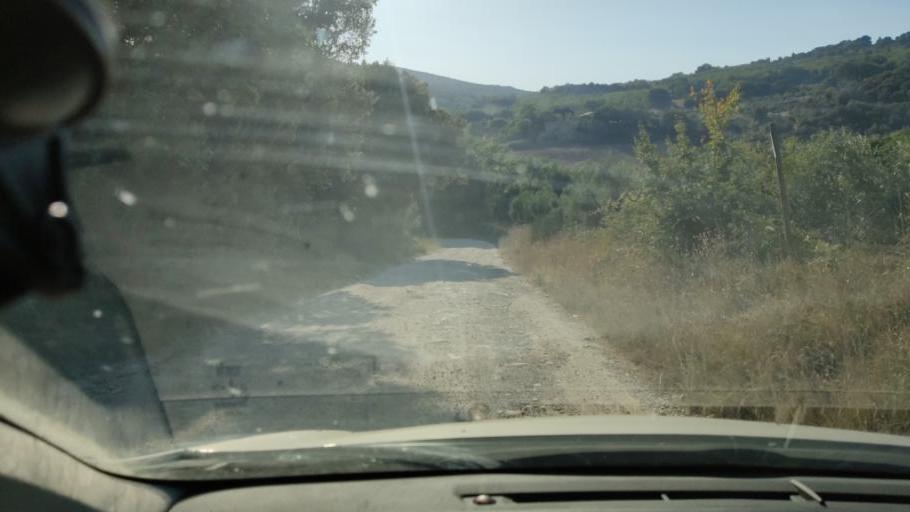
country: IT
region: Umbria
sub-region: Provincia di Terni
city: Amelia
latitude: 42.5455
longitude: 12.3910
